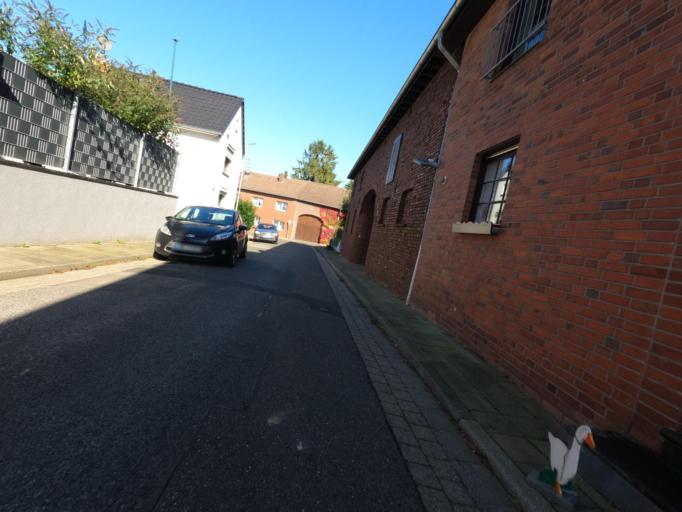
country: DE
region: North Rhine-Westphalia
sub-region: Regierungsbezirk Koln
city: Linnich
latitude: 50.9924
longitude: 6.2934
